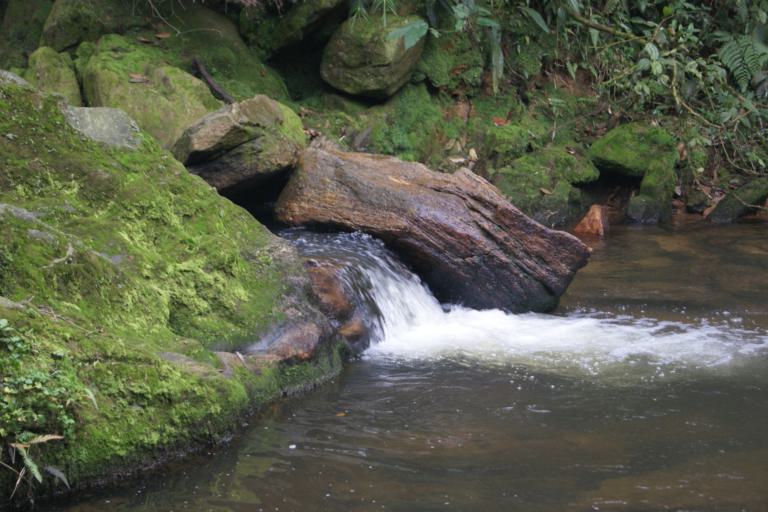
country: BR
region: Sao Paulo
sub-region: Rio Grande Da Serra
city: Rio Grande da Serra
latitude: -23.7873
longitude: -46.3616
